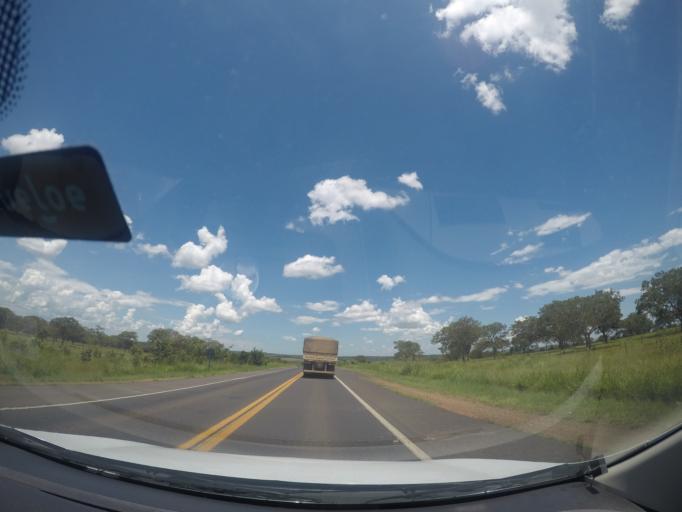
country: BR
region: Minas Gerais
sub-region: Prata
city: Prata
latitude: -19.3320
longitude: -48.9043
